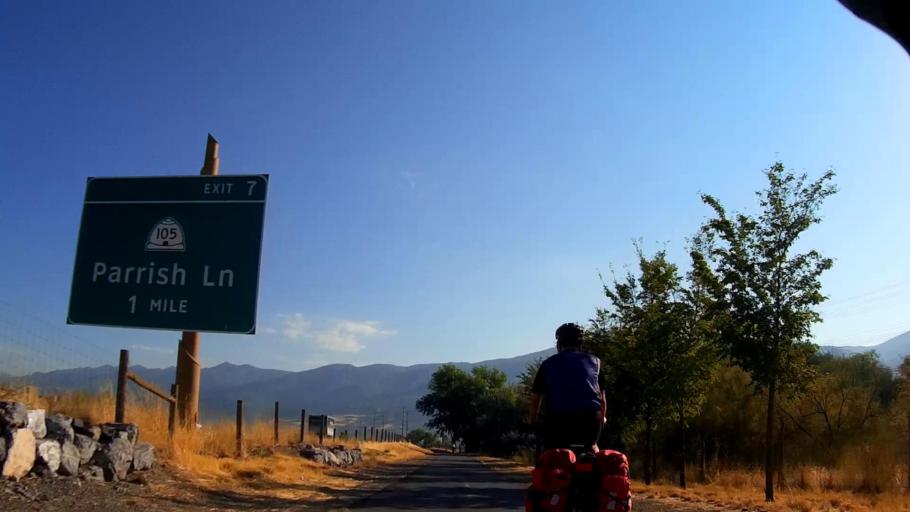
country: US
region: Utah
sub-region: Davis County
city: West Bountiful
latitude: 40.9075
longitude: -111.9159
